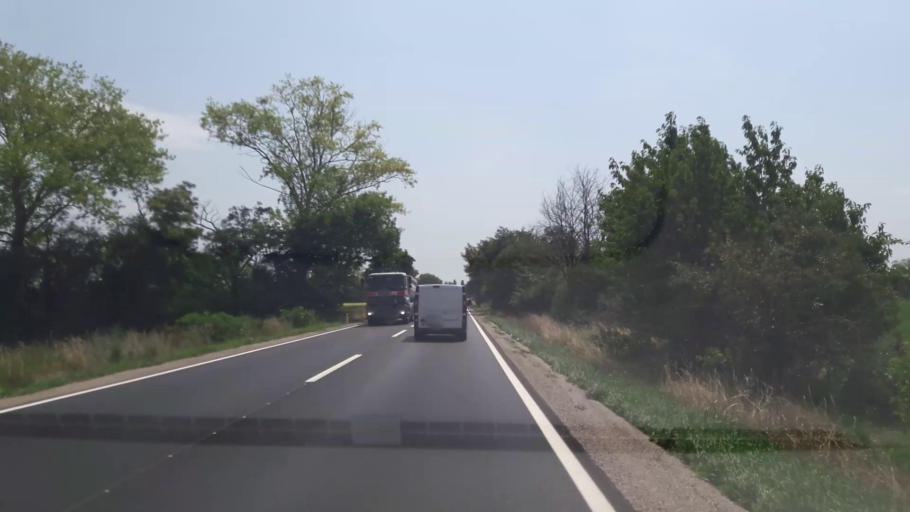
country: AT
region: Lower Austria
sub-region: Politischer Bezirk Wien-Umgebung
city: Rauchenwarth
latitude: 48.1170
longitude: 16.5165
